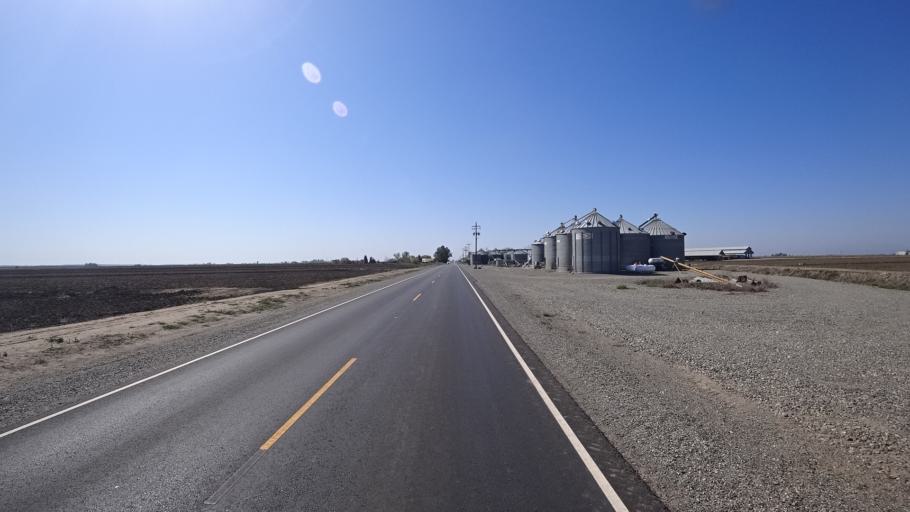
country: US
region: California
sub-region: Glenn County
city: Hamilton City
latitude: 39.6216
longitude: -122.0650
